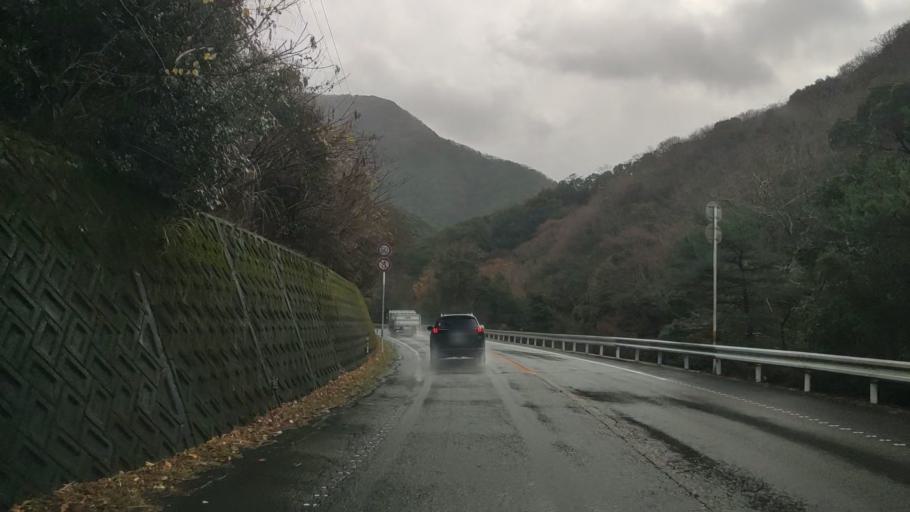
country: JP
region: Tokushima
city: Kamojimacho-jogejima
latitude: 34.1622
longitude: 134.3535
